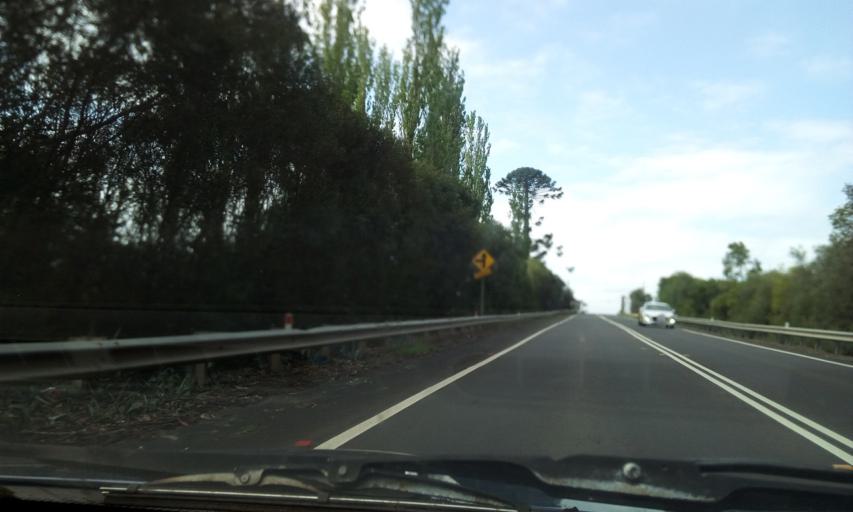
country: AU
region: New South Wales
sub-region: Campbelltown Municipality
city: Glen Alpine
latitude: -34.0914
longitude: 150.7718
